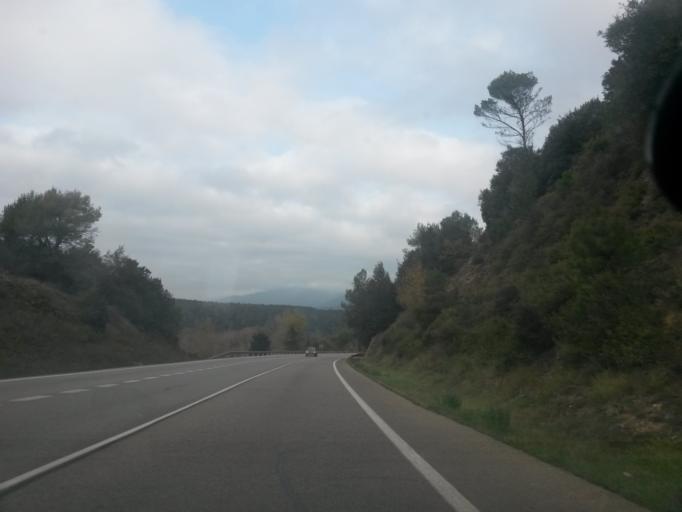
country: ES
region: Catalonia
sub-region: Provincia de Girona
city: Besalu
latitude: 42.1705
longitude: 2.7399
